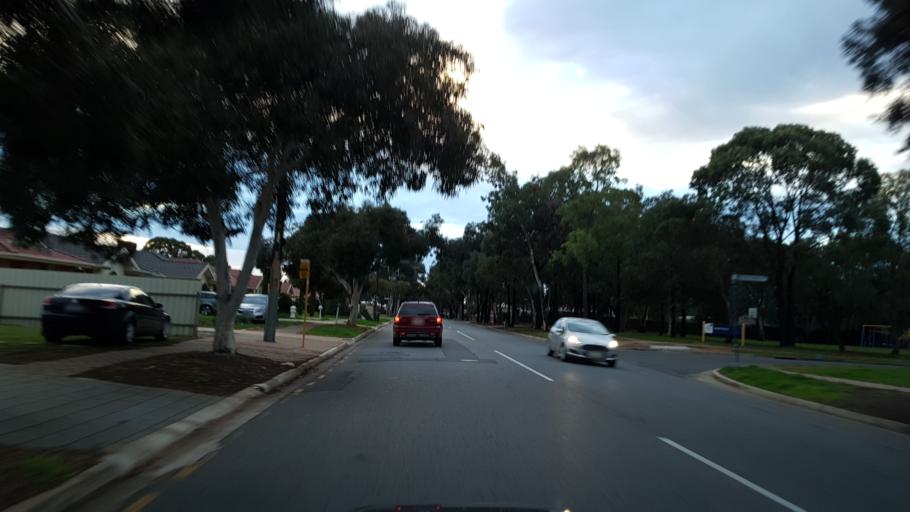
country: AU
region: South Australia
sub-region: Salisbury
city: Salisbury
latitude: -34.7600
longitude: 138.6162
